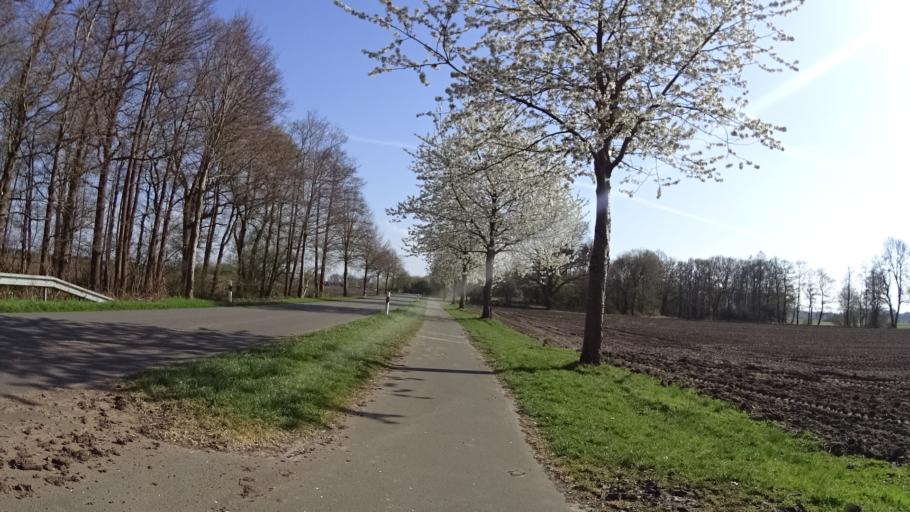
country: DE
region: Lower Saxony
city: Dorpen
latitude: 52.9457
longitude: 7.3159
